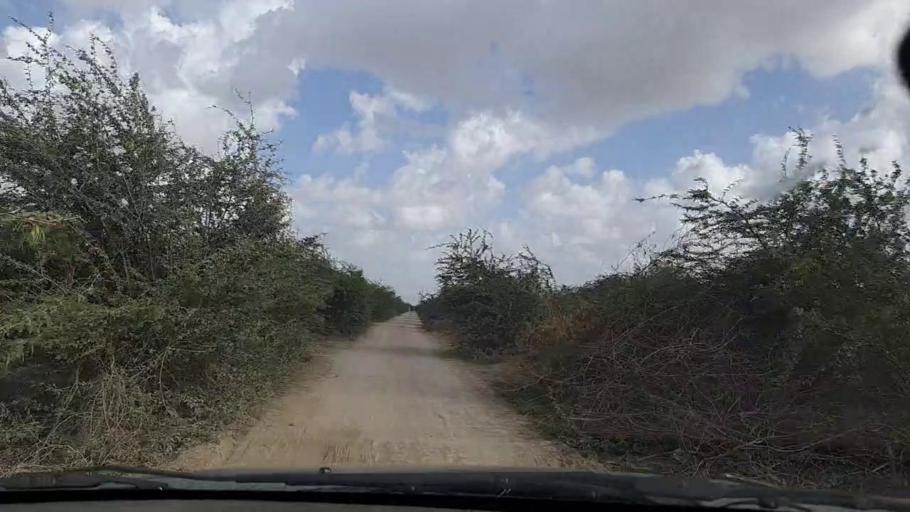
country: PK
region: Sindh
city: Keti Bandar
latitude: 24.0894
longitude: 67.6137
